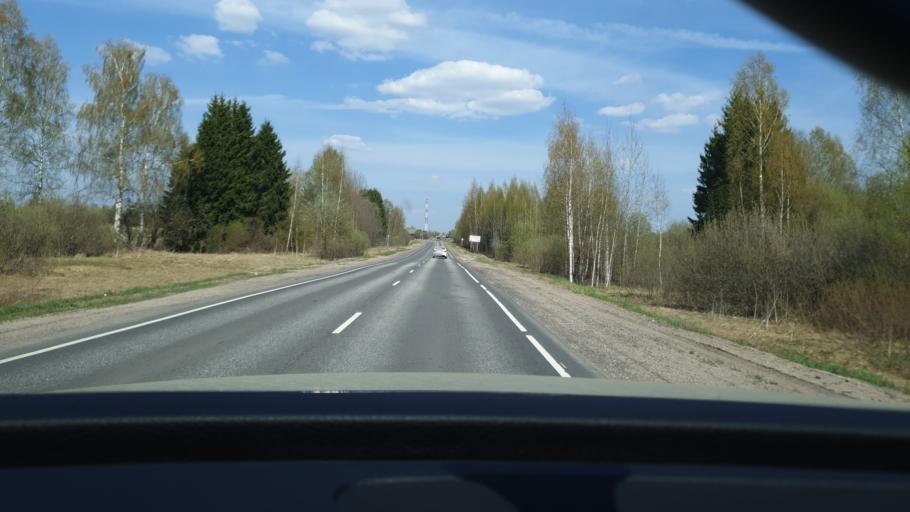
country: RU
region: Moskovskaya
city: Mikulino
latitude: 56.5187
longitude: 35.7155
